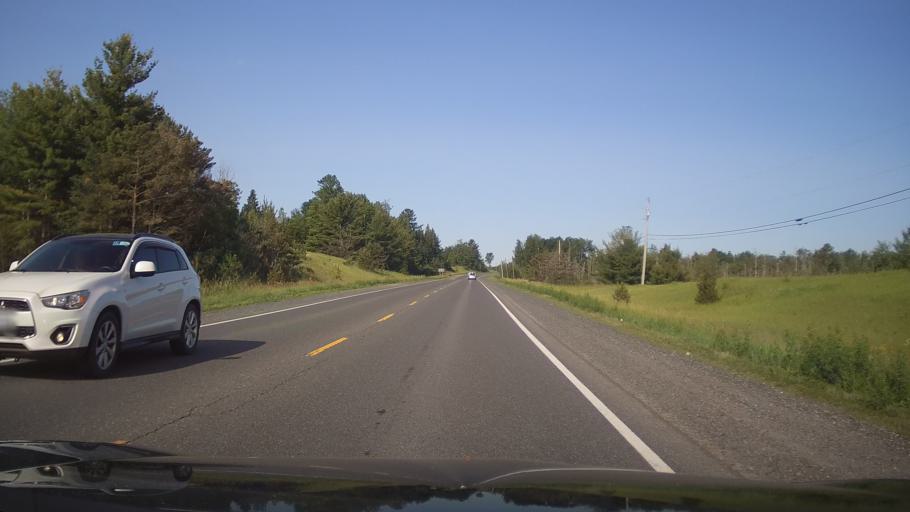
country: CA
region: Ontario
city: Quinte West
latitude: 44.4528
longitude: -77.7783
